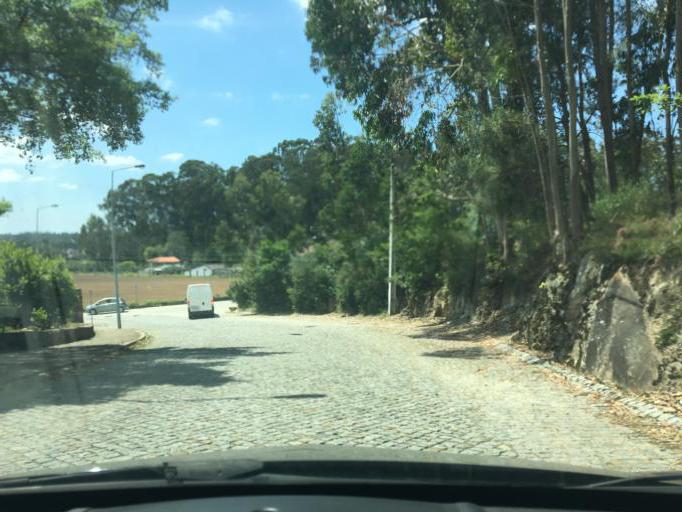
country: PT
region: Porto
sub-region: Maia
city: Anta
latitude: 41.2875
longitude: -8.6153
